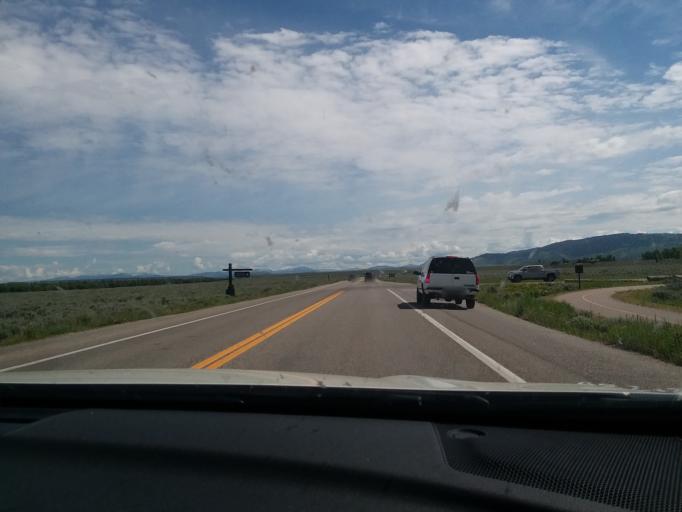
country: US
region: Wyoming
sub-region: Teton County
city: Jackson
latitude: 43.6646
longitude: -110.6956
